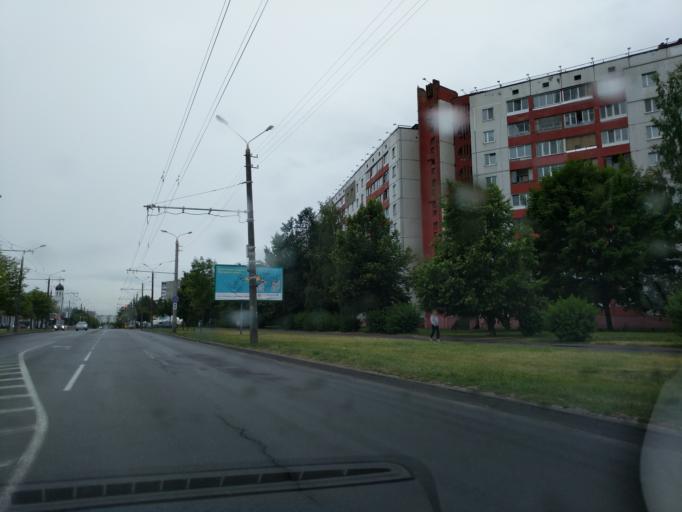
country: BY
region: Minsk
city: Novoye Medvezhino
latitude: 53.8634
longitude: 27.4803
